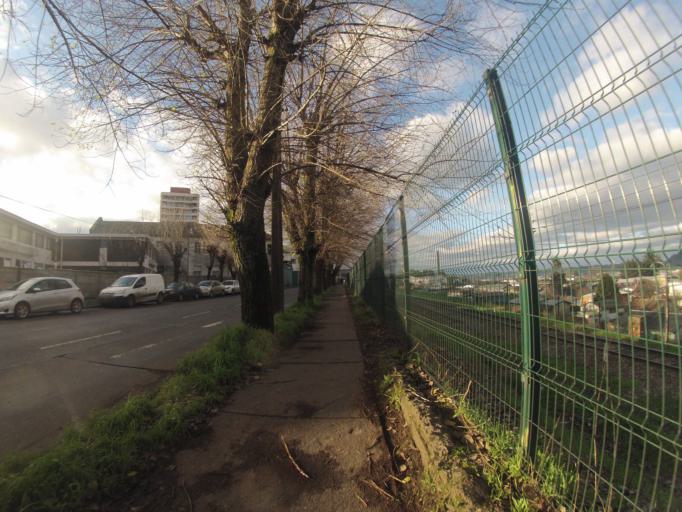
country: CL
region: Araucania
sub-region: Provincia de Cautin
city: Temuco
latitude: -38.7412
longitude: -72.5849
